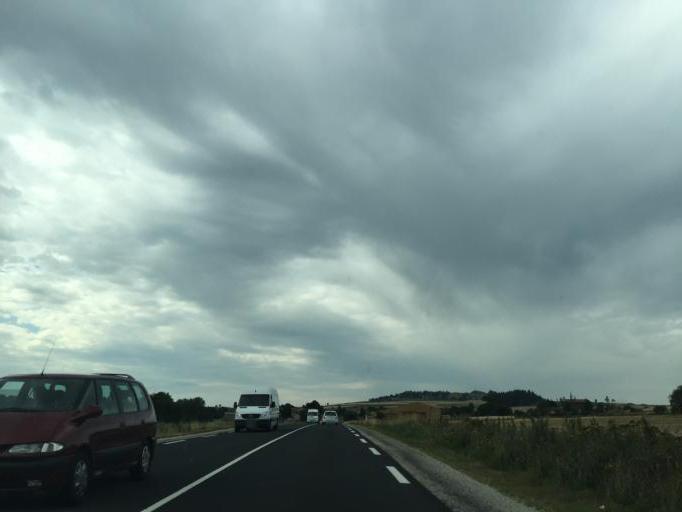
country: FR
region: Auvergne
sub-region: Departement de la Haute-Loire
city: Solignac-sur-Loire
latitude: 44.8843
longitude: 3.8472
